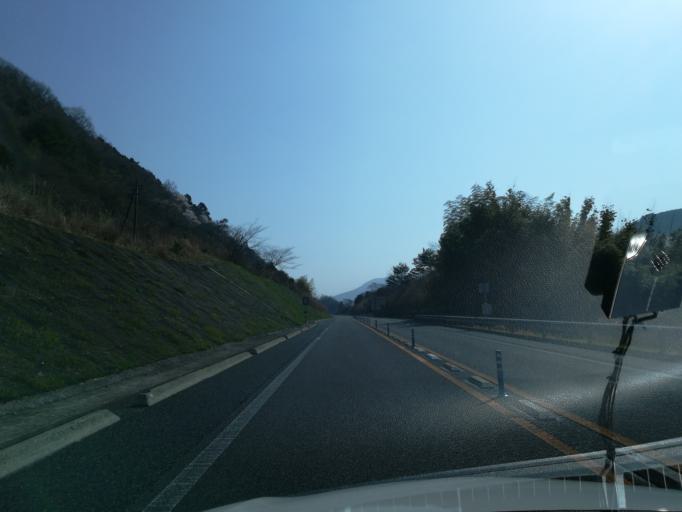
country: JP
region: Tokushima
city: Ikedacho
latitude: 34.0117
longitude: 133.7381
